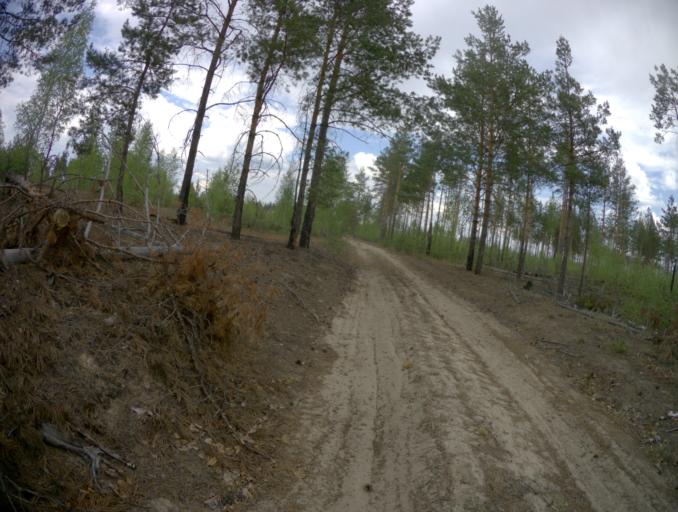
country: RU
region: Ivanovo
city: Talitsy
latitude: 56.4453
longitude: 42.2714
